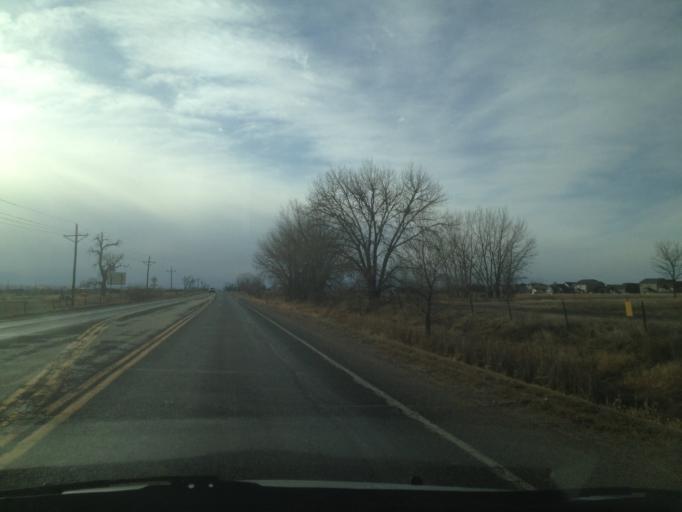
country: US
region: Colorado
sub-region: Weld County
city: Fort Lupton
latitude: 40.0803
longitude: -104.7834
